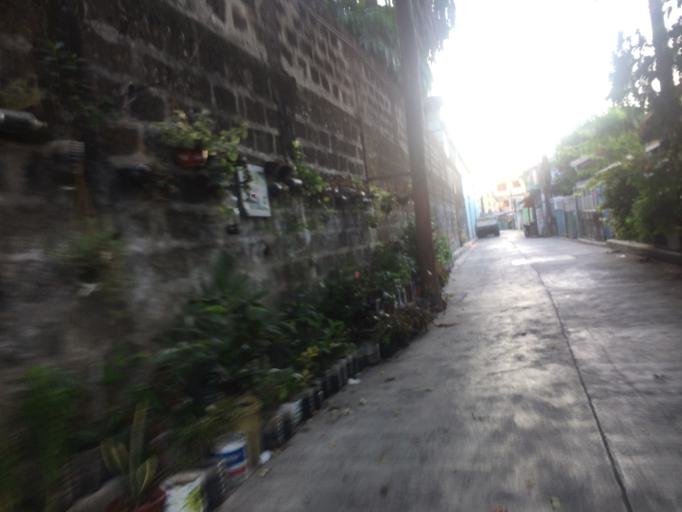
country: PH
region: Calabarzon
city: Bagong Pagasa
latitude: 14.6781
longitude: 121.0218
